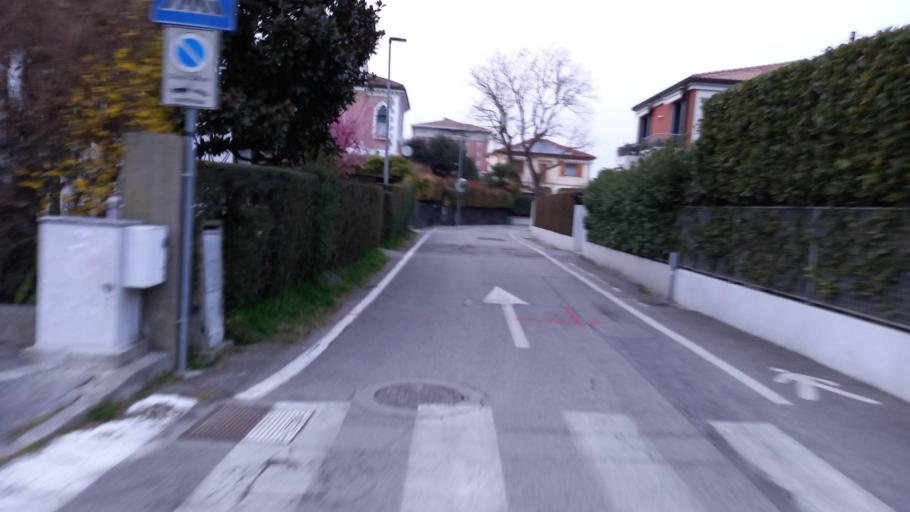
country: IT
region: Veneto
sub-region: Provincia di Treviso
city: Mogliano Veneto
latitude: 45.5594
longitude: 12.2320
